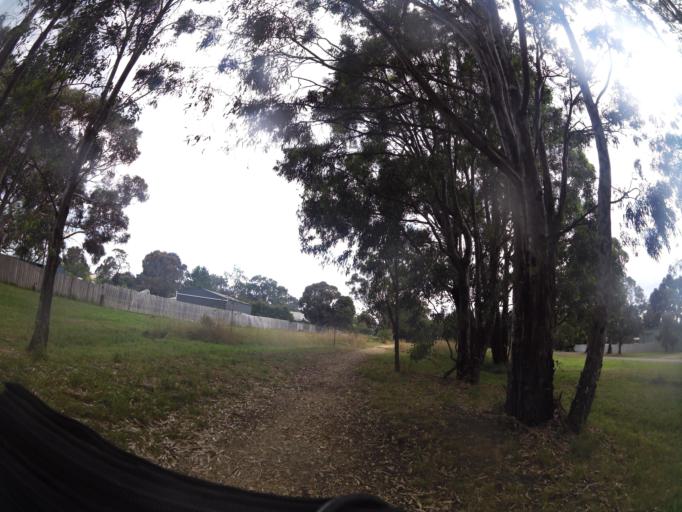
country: AU
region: Victoria
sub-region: Latrobe
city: Traralgon
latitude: -38.0589
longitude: 146.6268
